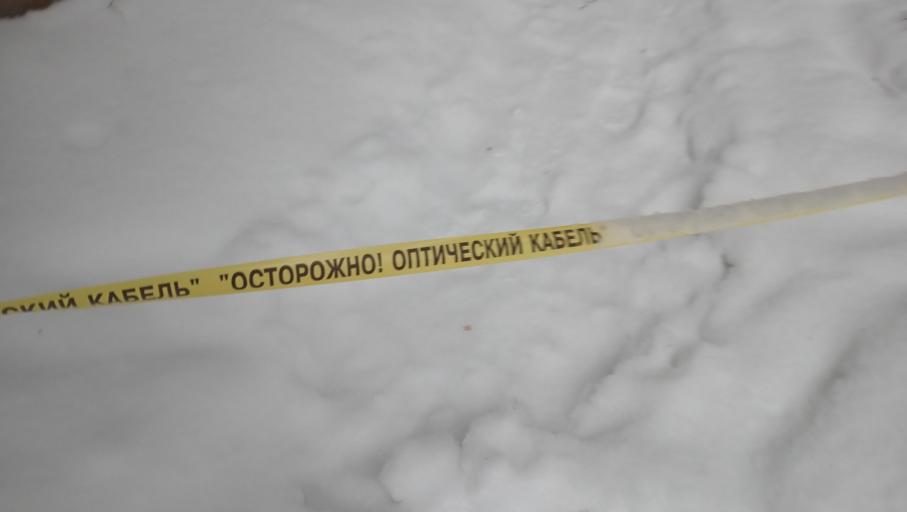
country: RU
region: Udmurtiya
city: Izhevsk
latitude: 56.9227
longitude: 53.2139
